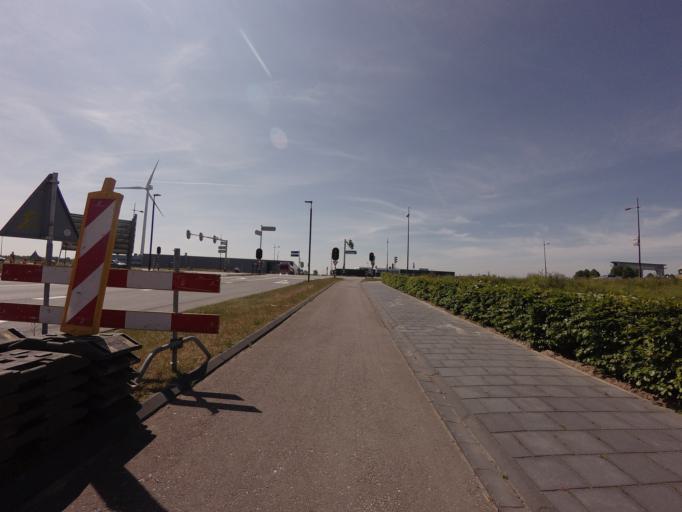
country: NL
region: Utrecht
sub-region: Gemeente Vianen
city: Vianen
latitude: 52.0148
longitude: 5.1151
